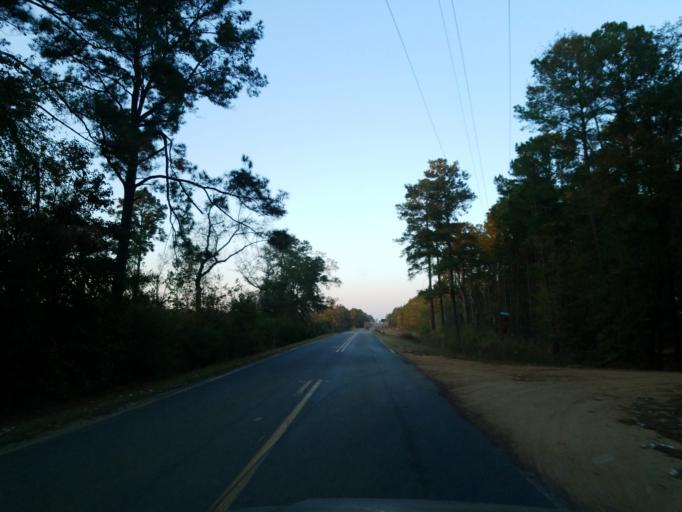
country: US
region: Georgia
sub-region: Ben Hill County
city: Fitzgerald
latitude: 31.6950
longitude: -83.3852
